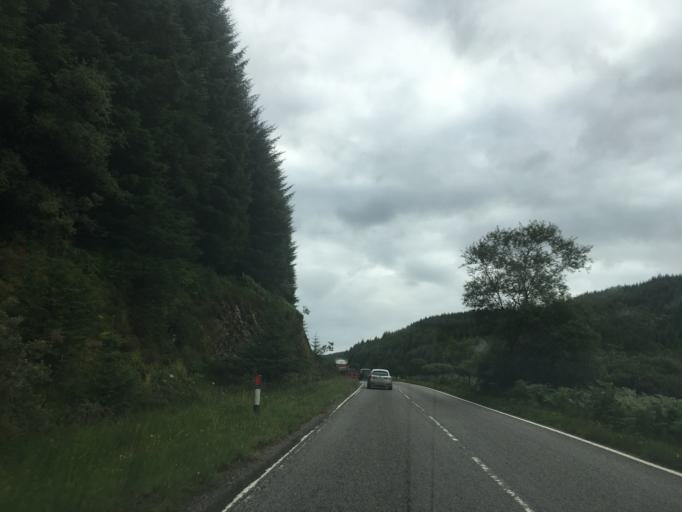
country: GB
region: Scotland
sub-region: Argyll and Bute
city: Oban
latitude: 56.2886
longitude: -5.4726
